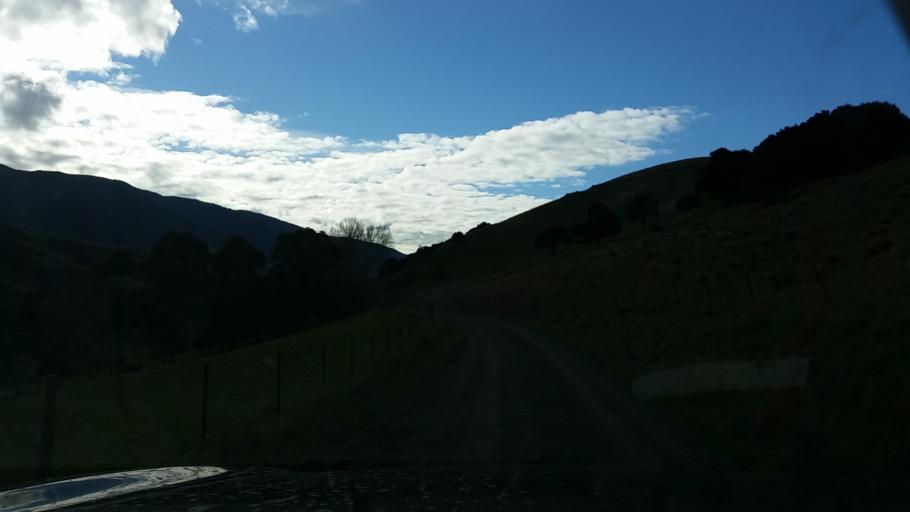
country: NZ
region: Marlborough
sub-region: Marlborough District
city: Blenheim
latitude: -41.7695
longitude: 173.8576
